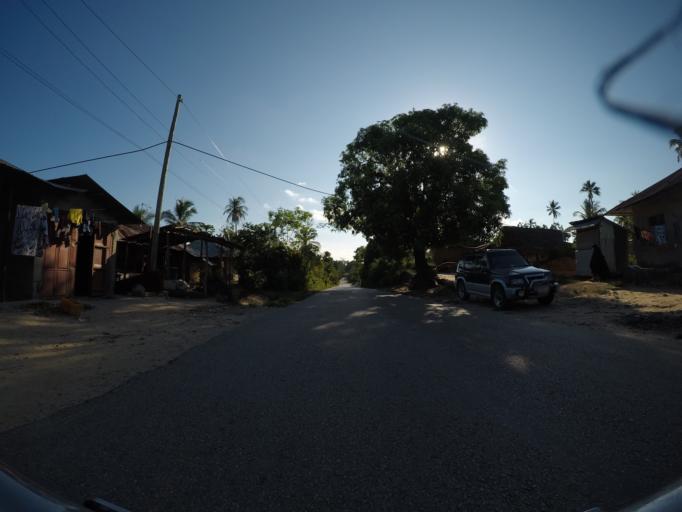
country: TZ
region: Pemba South
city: Chake Chake
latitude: -5.2974
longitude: 39.7584
